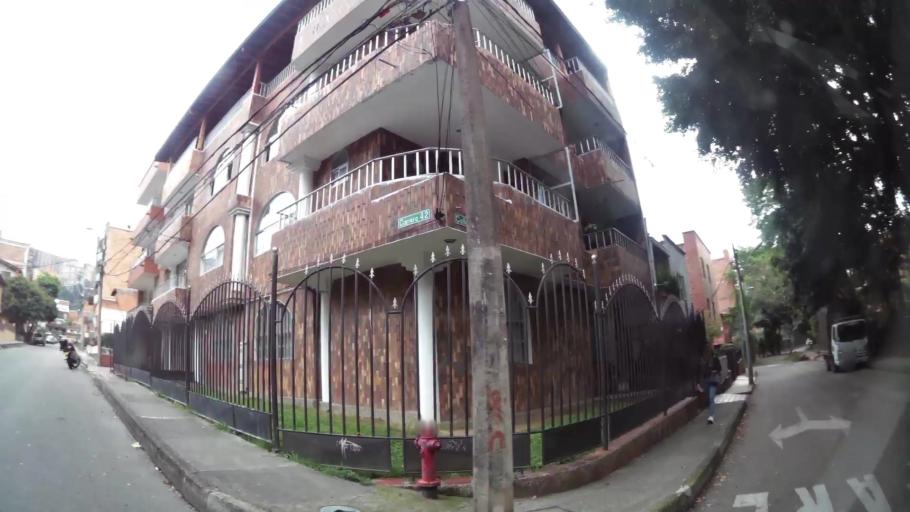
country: CO
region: Antioquia
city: Envigado
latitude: 6.1612
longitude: -75.5941
